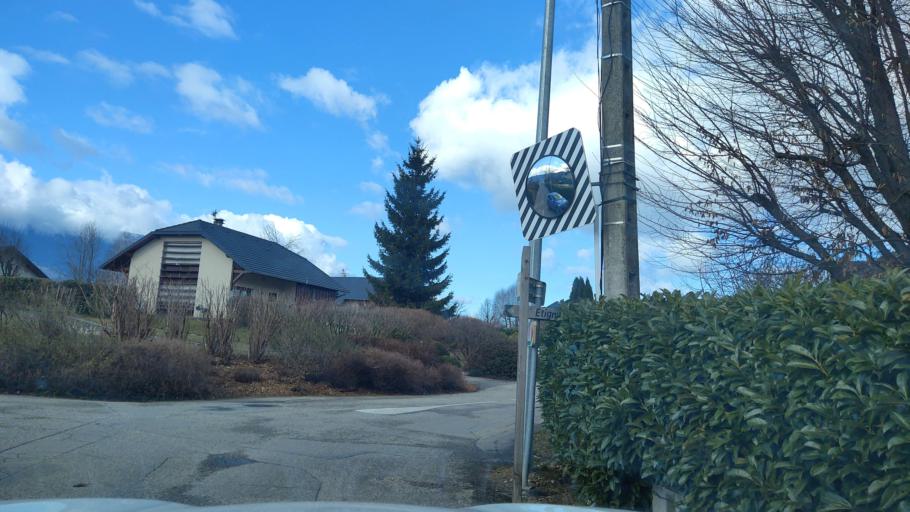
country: FR
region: Rhone-Alpes
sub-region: Departement de la Savoie
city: Sonnaz
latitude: 45.6118
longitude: 5.9080
